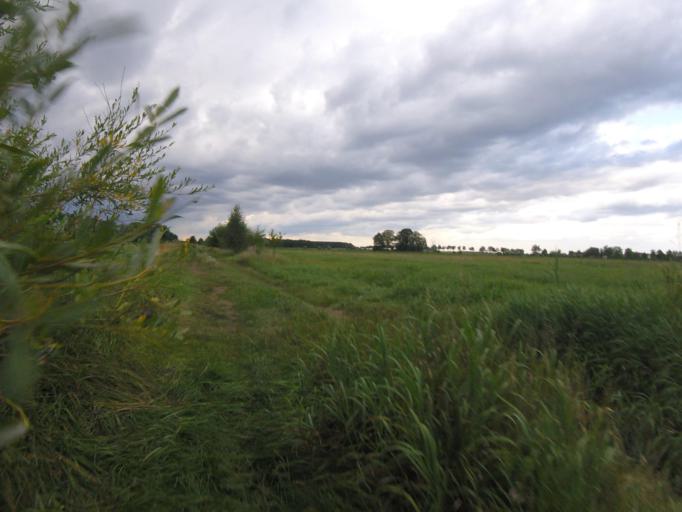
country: DE
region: Brandenburg
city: Mittenwalde
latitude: 52.2750
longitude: 13.5275
